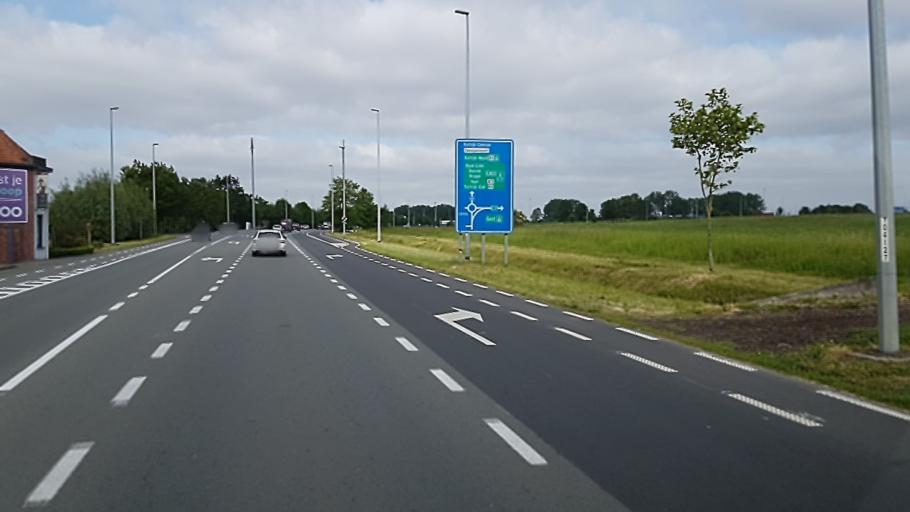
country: BE
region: Flanders
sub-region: Provincie West-Vlaanderen
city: Zwevegem
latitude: 50.8162
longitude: 3.3060
